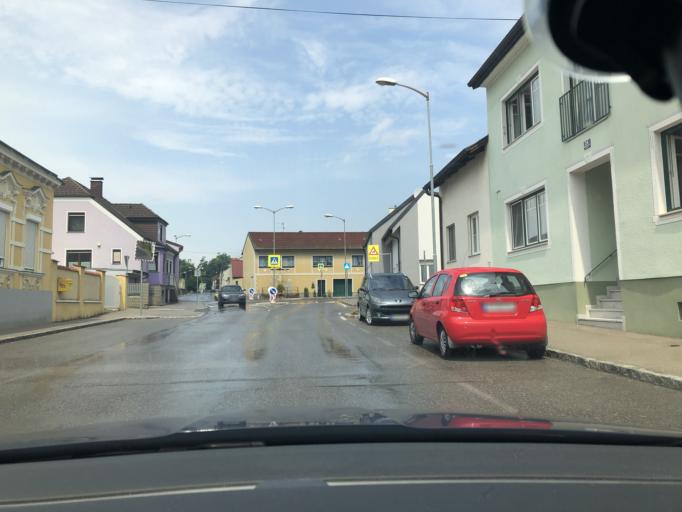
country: AT
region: Lower Austria
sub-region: Politischer Bezirk Mistelbach
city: Gaweinstal
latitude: 48.4784
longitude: 16.5878
